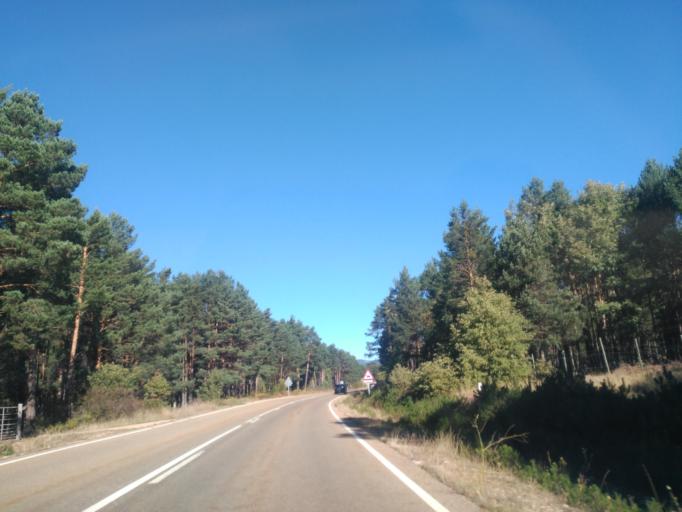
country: ES
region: Castille and Leon
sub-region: Provincia de Soria
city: Vinuesa
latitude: 41.9311
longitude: -2.7652
